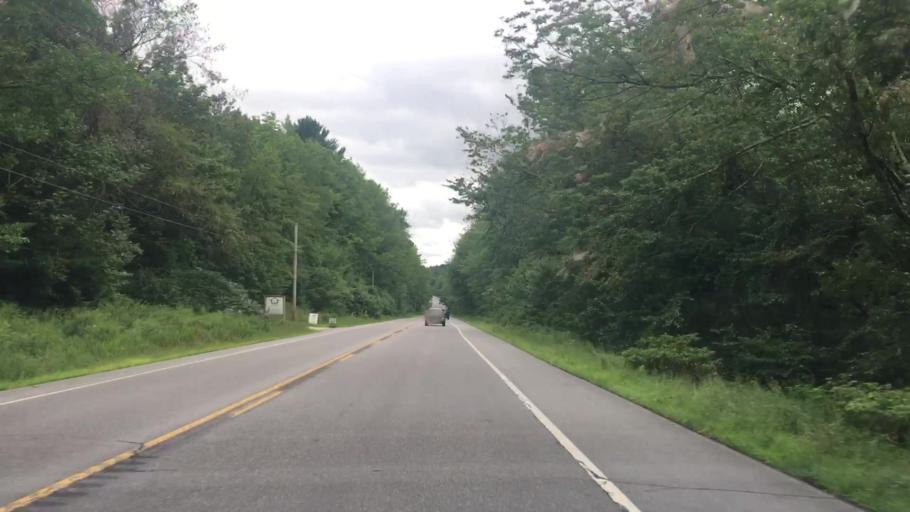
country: US
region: Maine
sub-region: York County
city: Alfred
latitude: 43.5009
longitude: -70.7181
